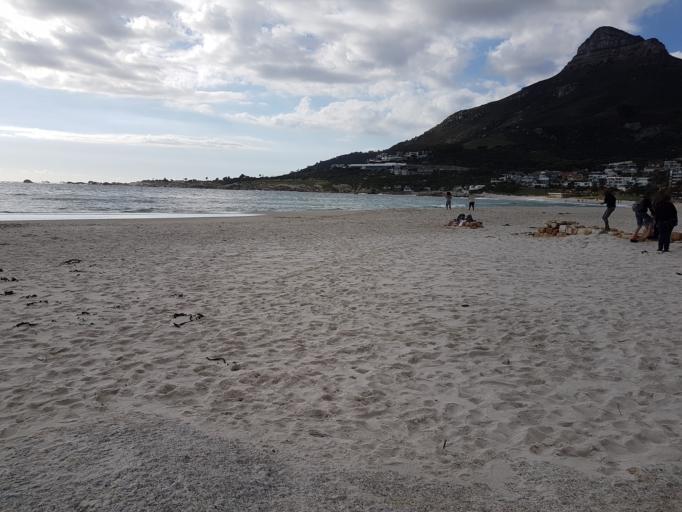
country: ZA
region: Western Cape
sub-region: City of Cape Town
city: Cape Town
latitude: -33.9530
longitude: 18.3757
